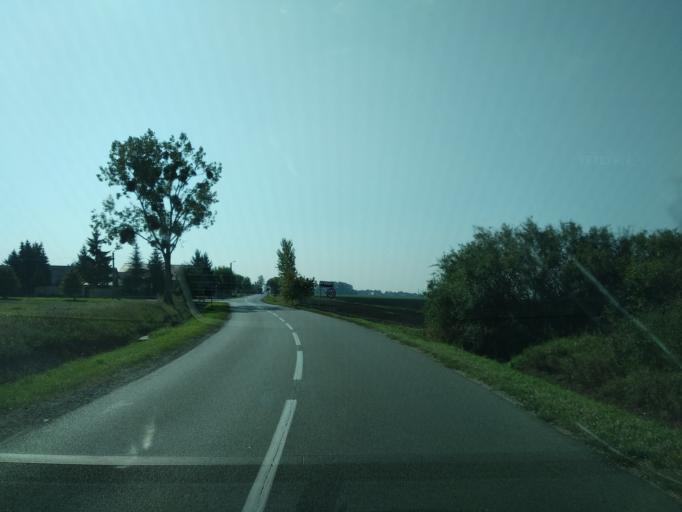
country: PL
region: Lower Silesian Voivodeship
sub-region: Powiat wroclawski
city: Zerniki Wroclawskie
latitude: 51.0365
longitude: 17.0298
